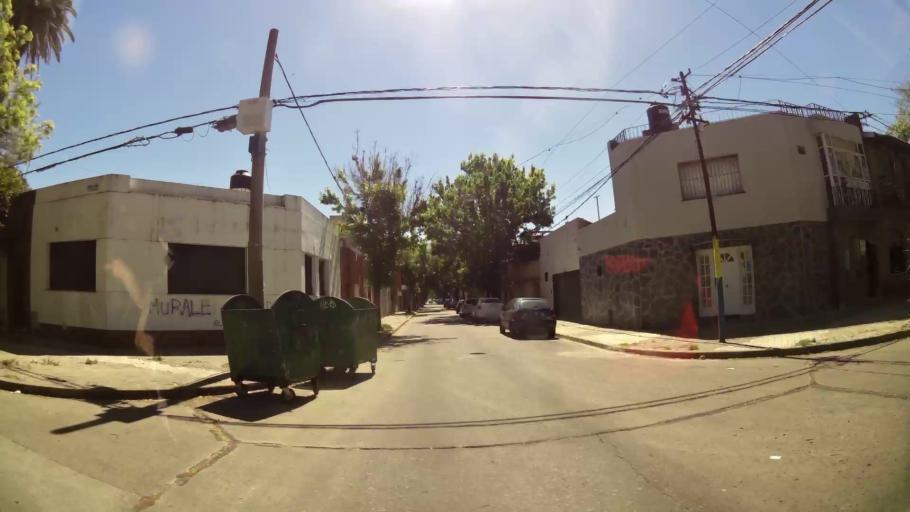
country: AR
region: Santa Fe
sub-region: Departamento de Rosario
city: Rosario
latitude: -32.9431
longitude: -60.6830
